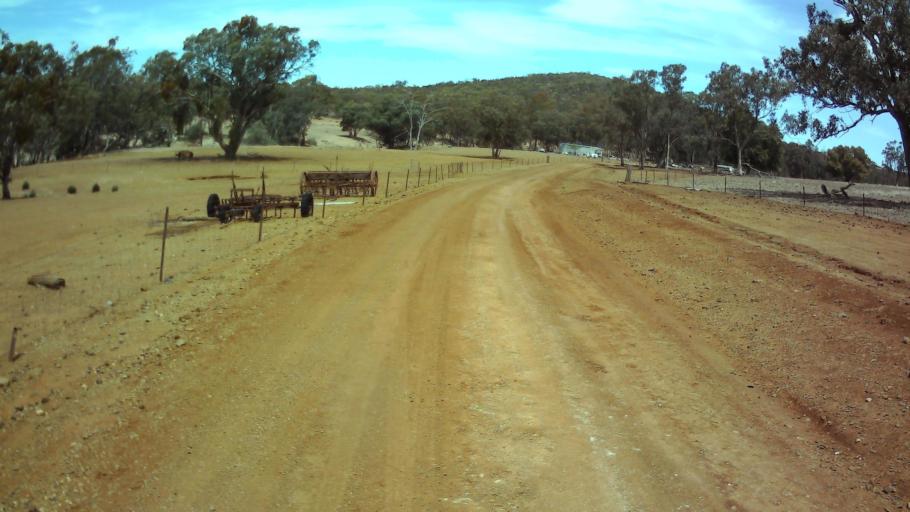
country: AU
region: New South Wales
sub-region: Weddin
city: Grenfell
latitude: -33.7908
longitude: 148.1592
